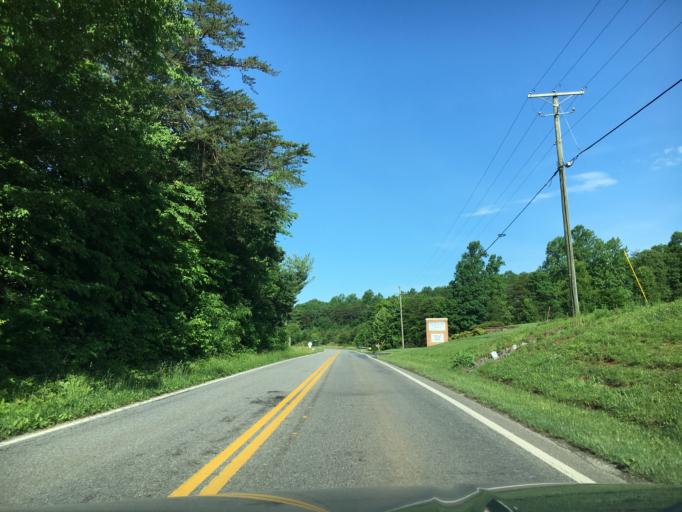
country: US
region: Virginia
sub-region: Campbell County
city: Rustburg
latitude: 37.3128
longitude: -79.1746
